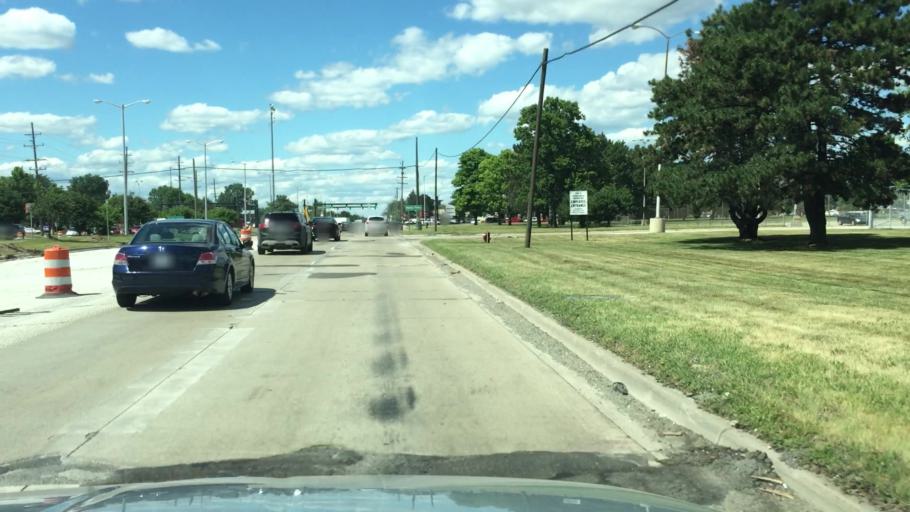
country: US
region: Michigan
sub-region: Macomb County
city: Sterling Heights
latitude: 42.5630
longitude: -83.0488
